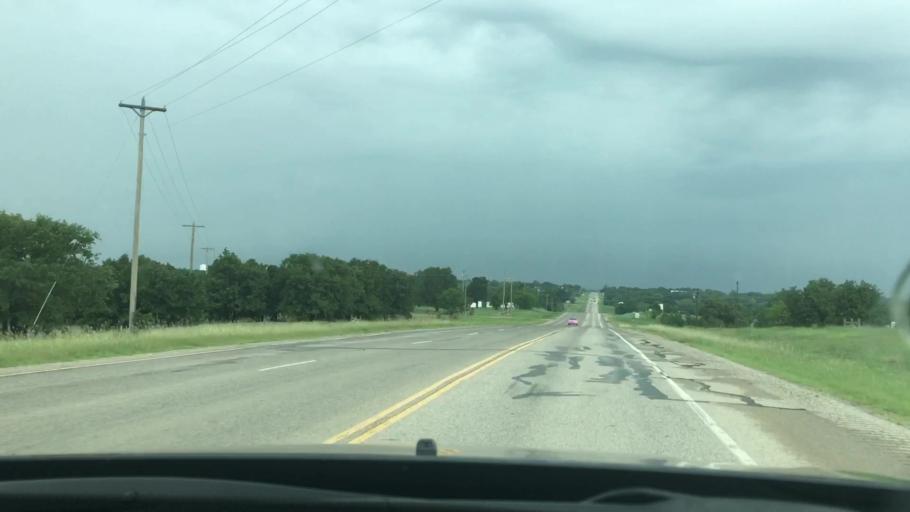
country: US
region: Oklahoma
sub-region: Carter County
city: Healdton
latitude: 34.1997
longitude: -97.4747
